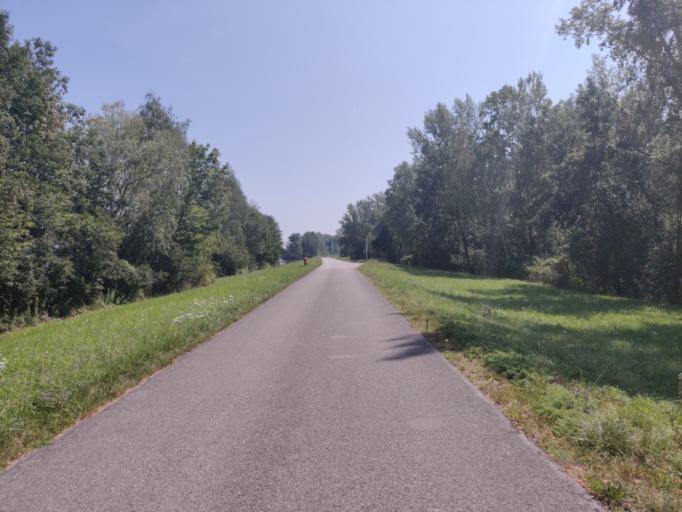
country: AT
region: Upper Austria
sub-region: Politischer Bezirk Urfahr-Umgebung
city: Feldkirchen an der Donau
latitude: 48.3252
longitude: 14.0457
